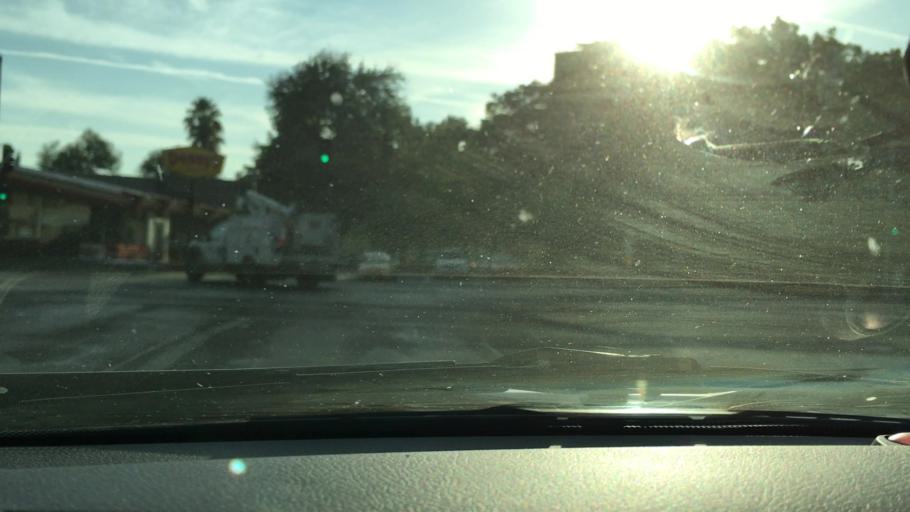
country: US
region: California
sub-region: Stanislaus County
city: Modesto
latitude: 37.6456
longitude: -120.9940
